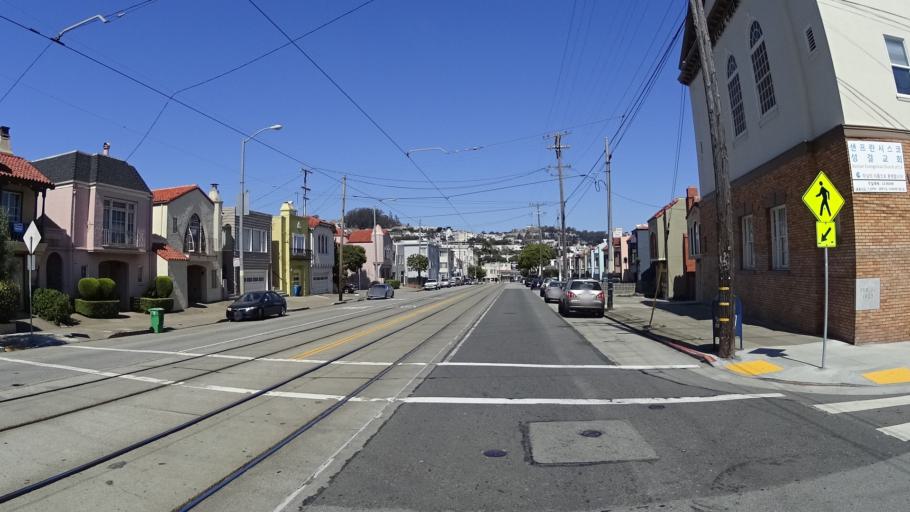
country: US
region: California
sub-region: San Mateo County
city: Daly City
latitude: 37.7269
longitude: -122.4414
